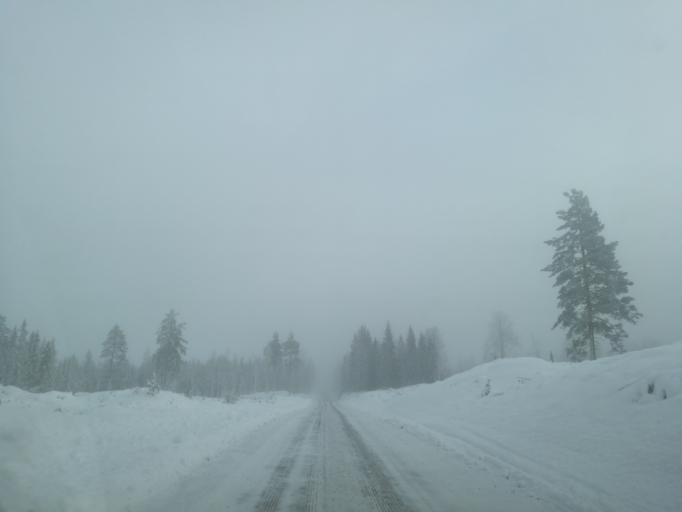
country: SE
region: Vaermland
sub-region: Torsby Kommun
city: Torsby
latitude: 60.6704
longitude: 12.8504
